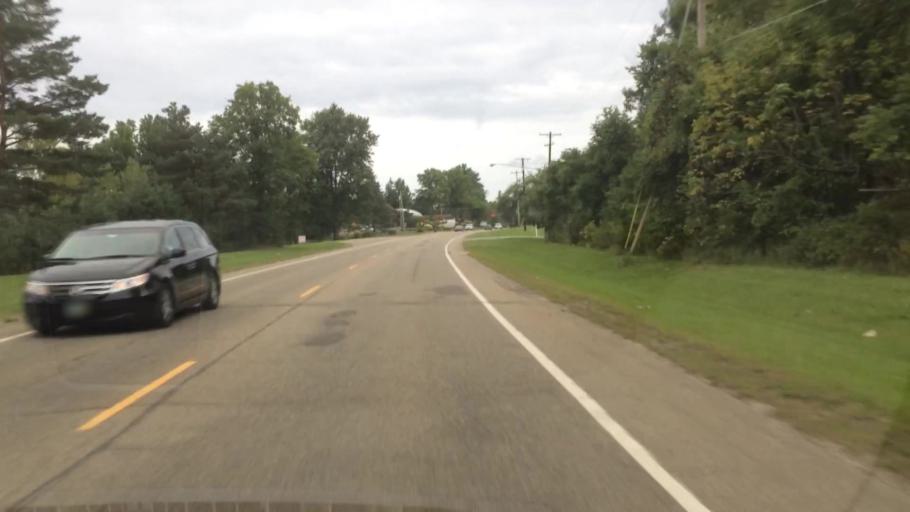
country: US
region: Ohio
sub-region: Summit County
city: Boston Heights
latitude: 41.2119
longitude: -81.4916
